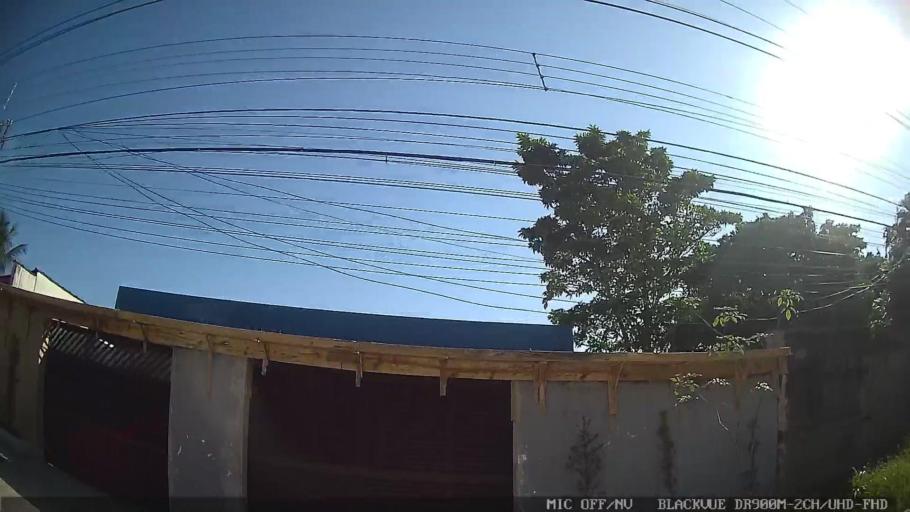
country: BR
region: Sao Paulo
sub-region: Guaruja
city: Guaruja
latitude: -23.9695
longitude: -46.2112
